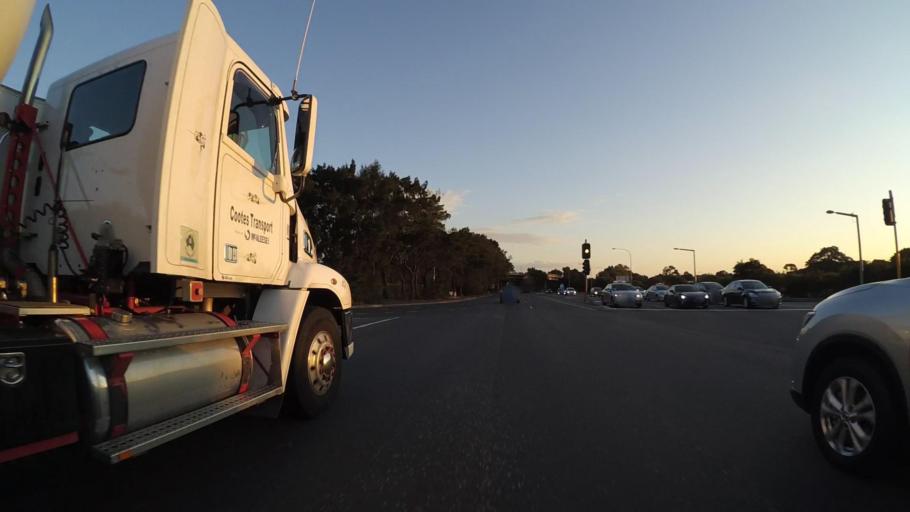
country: AU
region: New South Wales
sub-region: Botany Bay
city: Botany
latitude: -33.9382
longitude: 151.1929
